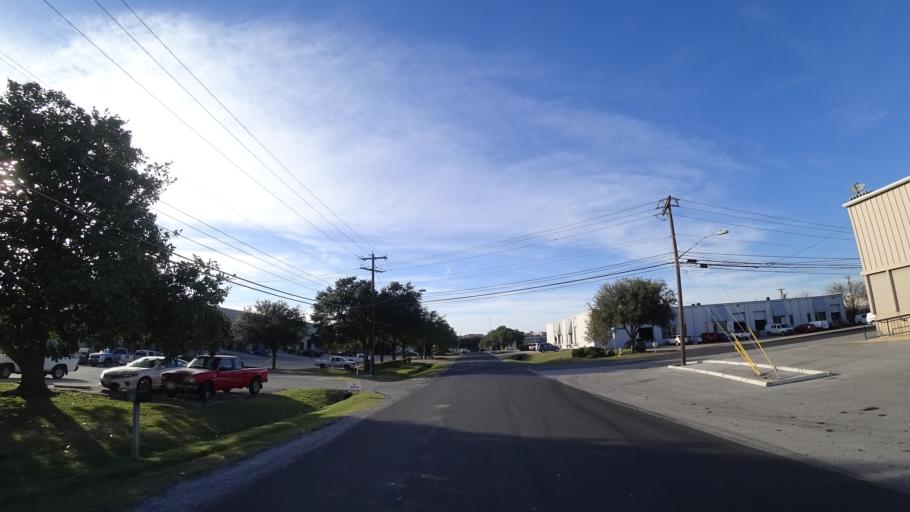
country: US
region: Texas
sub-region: Williamson County
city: Jollyville
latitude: 30.3803
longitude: -97.7303
